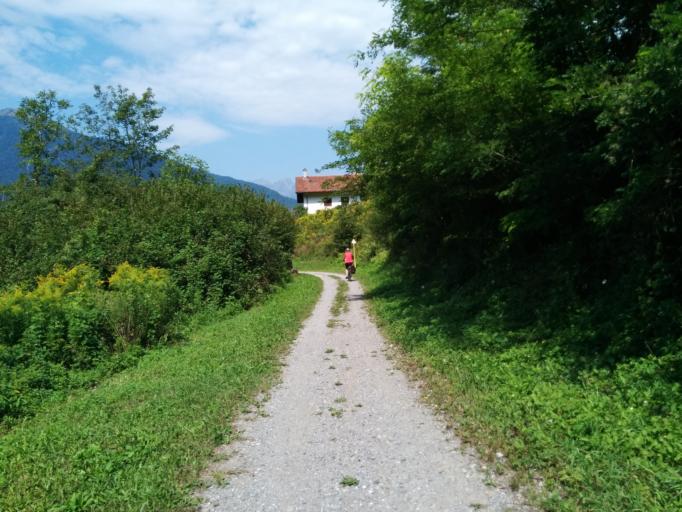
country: IT
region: Friuli Venezia Giulia
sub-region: Provincia di Udine
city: Ovaro
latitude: 46.4668
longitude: 12.8763
